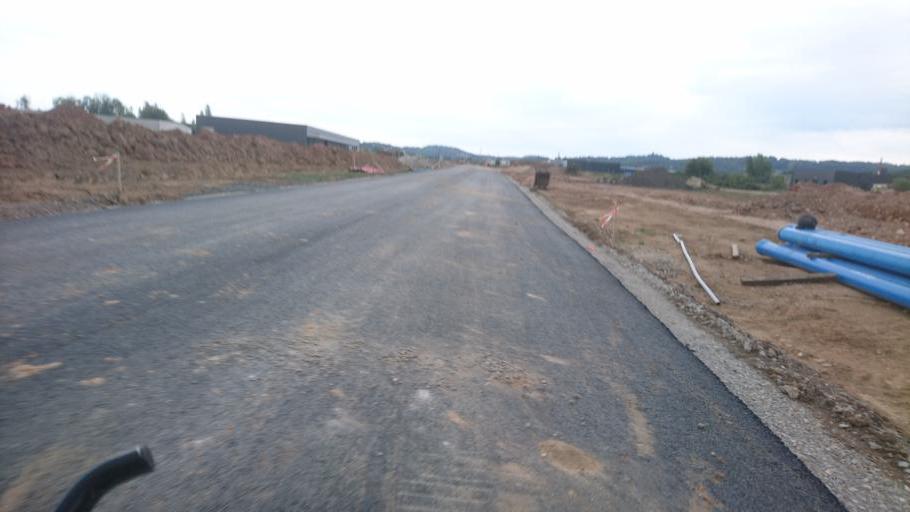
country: FR
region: Limousin
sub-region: Departement de la Correze
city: Saint-Pantaleon-de-Larche
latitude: 45.1558
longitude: 1.4656
